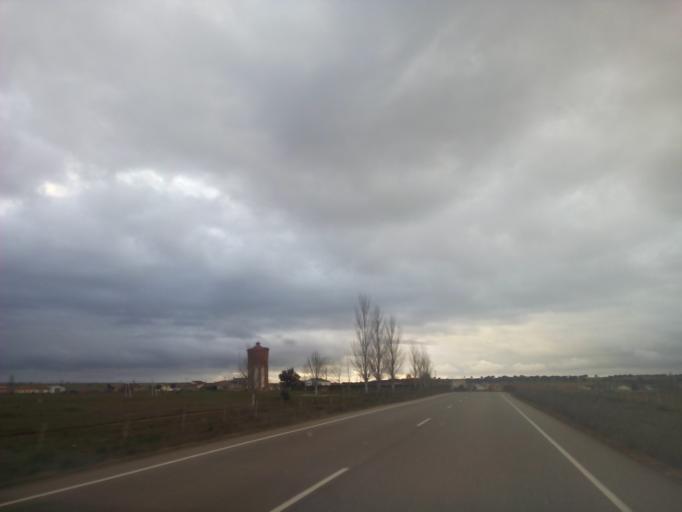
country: ES
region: Castille and Leon
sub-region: Provincia de Salamanca
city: Cabrillas
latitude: 40.7354
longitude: -6.1708
